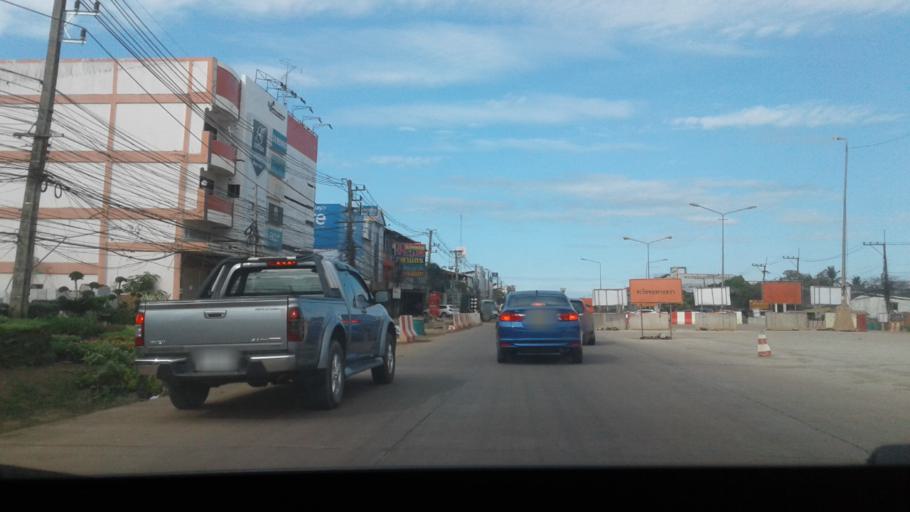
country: TH
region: Changwat Udon Thani
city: Udon Thani
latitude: 17.4300
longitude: 102.7911
